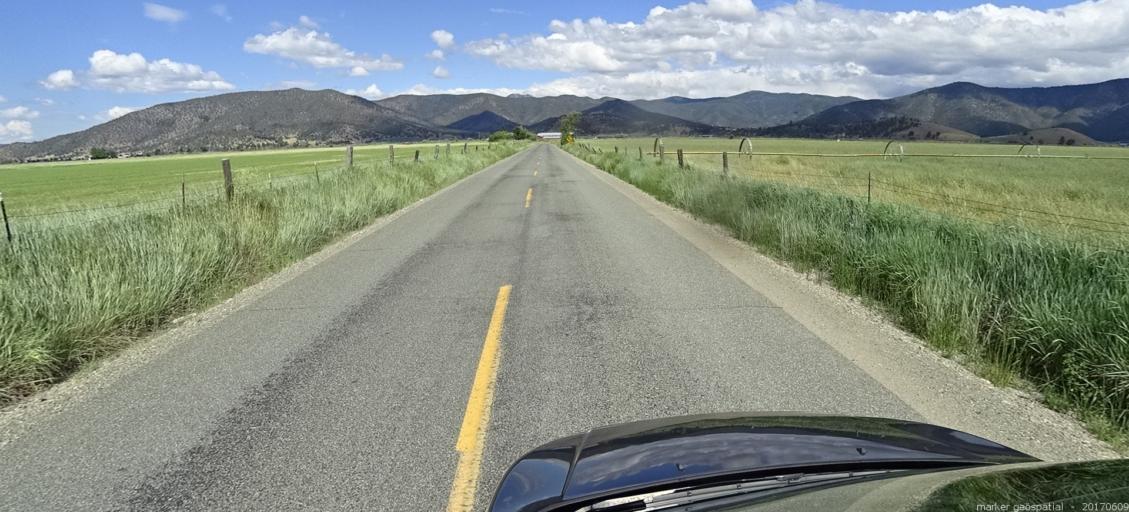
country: US
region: California
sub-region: Siskiyou County
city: Yreka
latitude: 41.4892
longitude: -122.8664
